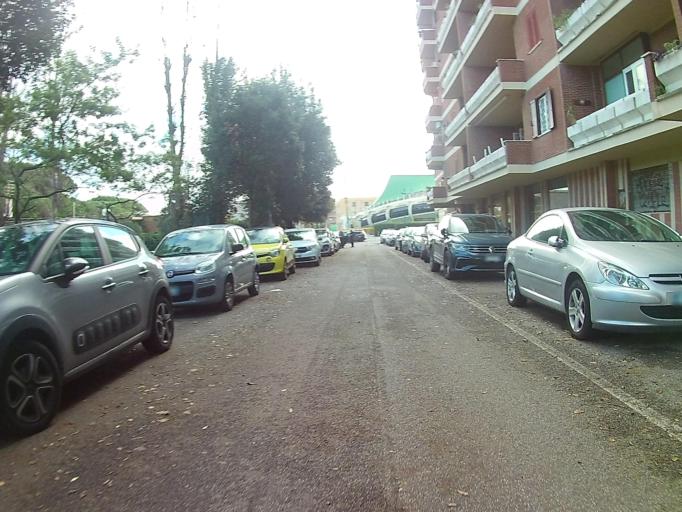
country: IT
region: Latium
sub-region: Citta metropolitana di Roma Capitale
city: Lido di Ostia
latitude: 41.7208
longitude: 12.3077
